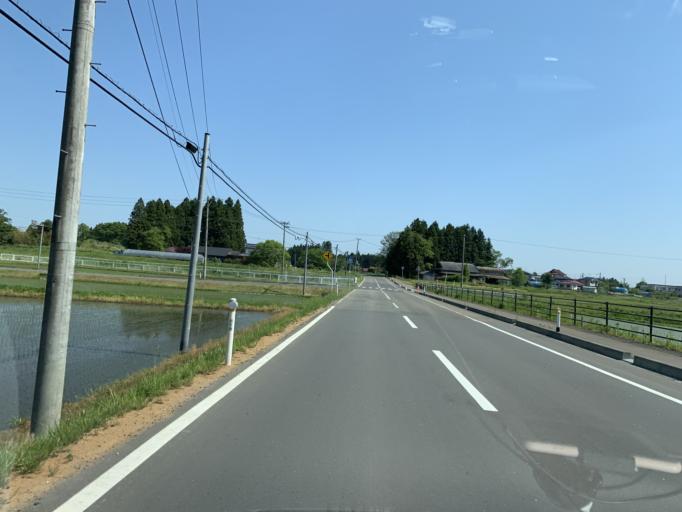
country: JP
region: Iwate
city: Mizusawa
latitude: 39.0953
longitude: 141.0751
